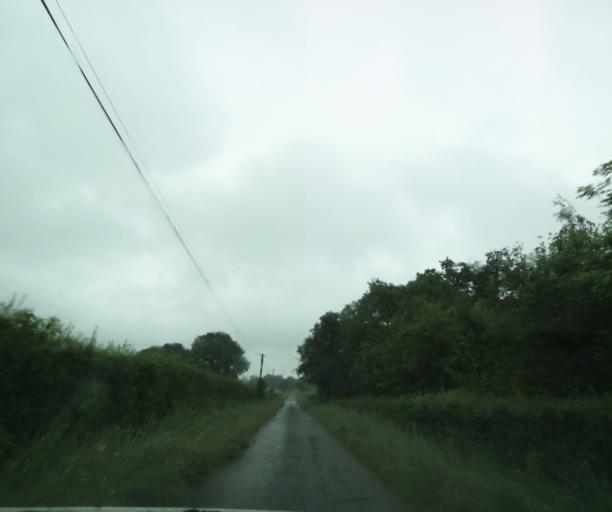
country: FR
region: Bourgogne
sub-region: Departement de Saone-et-Loire
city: Ciry-le-Noble
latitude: 46.5632
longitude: 4.3200
